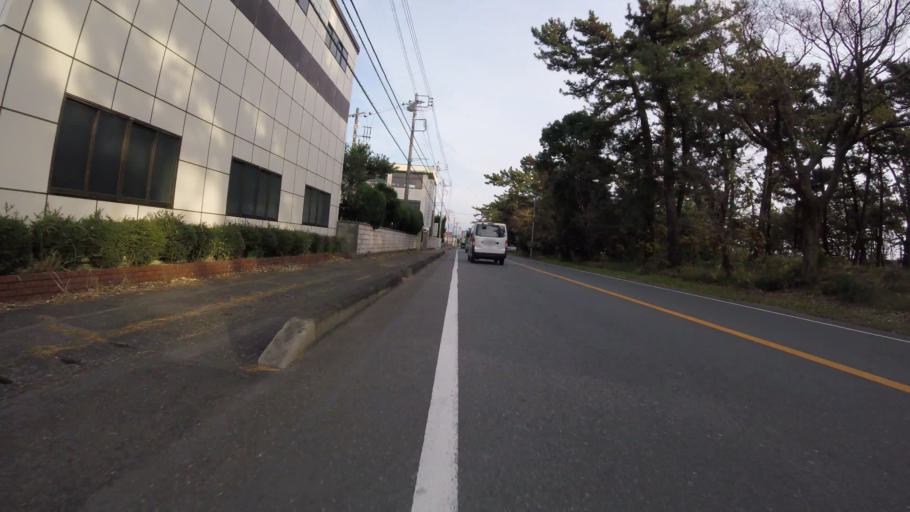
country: JP
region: Shizuoka
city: Fuji
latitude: 35.1300
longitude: 138.7703
